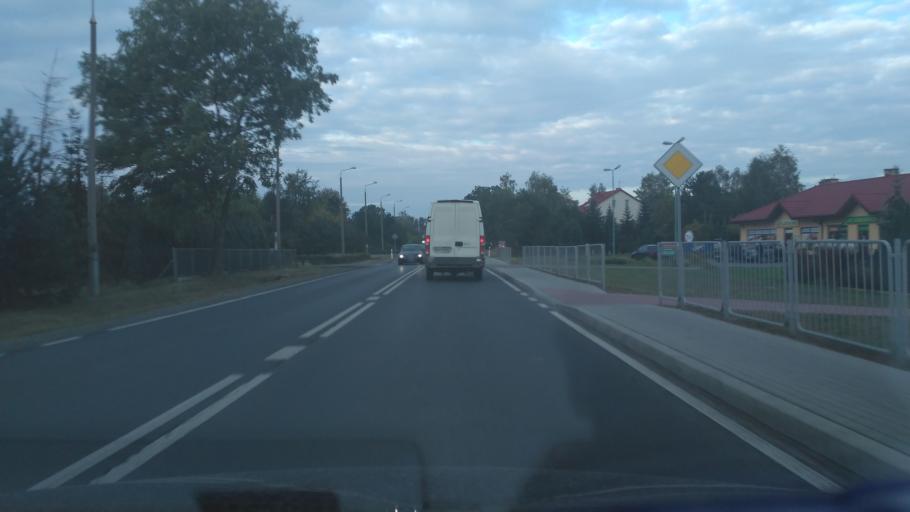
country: PL
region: Lublin Voivodeship
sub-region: Powiat leczynski
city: Spiczyn
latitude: 51.2990
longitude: 22.7211
